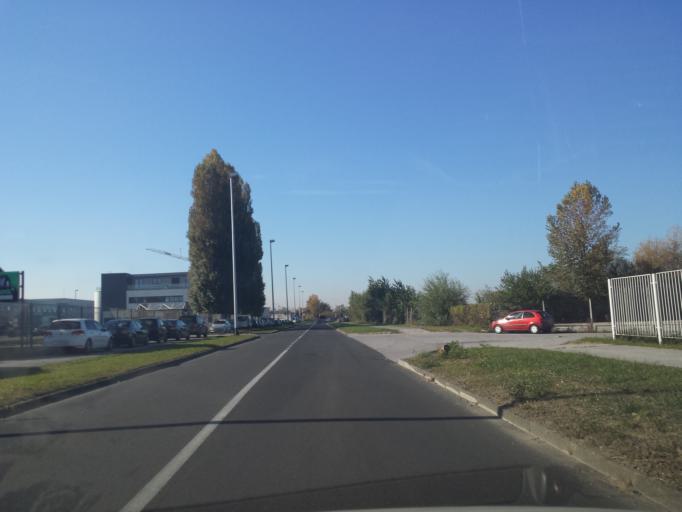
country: HR
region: Grad Zagreb
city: Jezdovec
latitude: 45.8079
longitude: 15.8480
